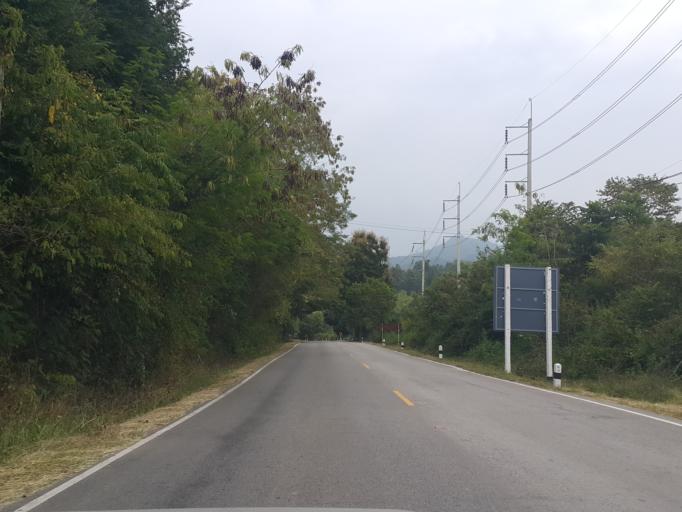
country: TH
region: Mae Hong Son
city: Mae Hi
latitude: 19.2854
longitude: 98.4776
